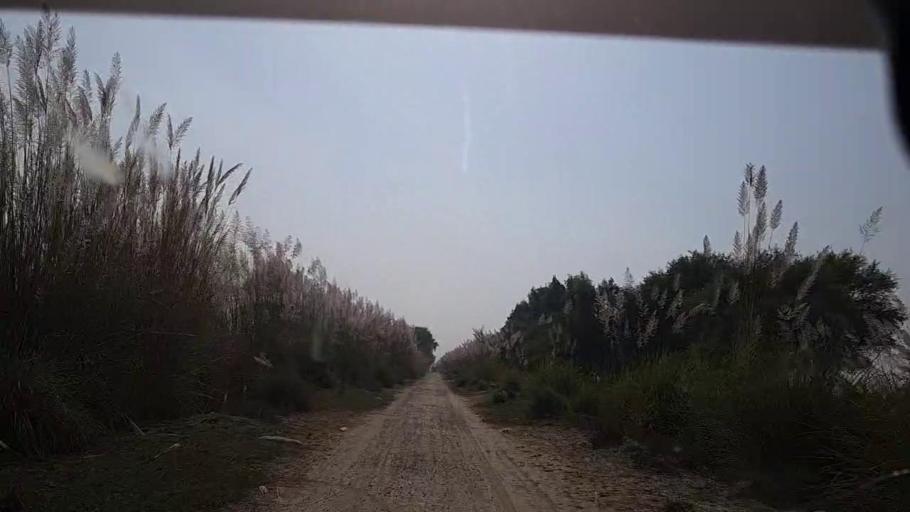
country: PK
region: Sindh
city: Shikarpur
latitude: 28.1206
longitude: 68.6613
